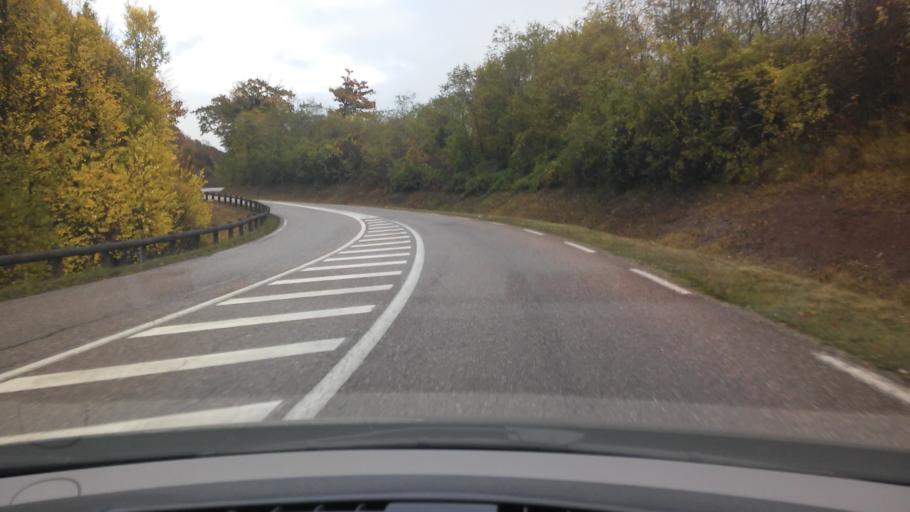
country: FR
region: Lorraine
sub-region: Departement de la Moselle
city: Kedange-sur-Canner
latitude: 49.2989
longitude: 6.3700
